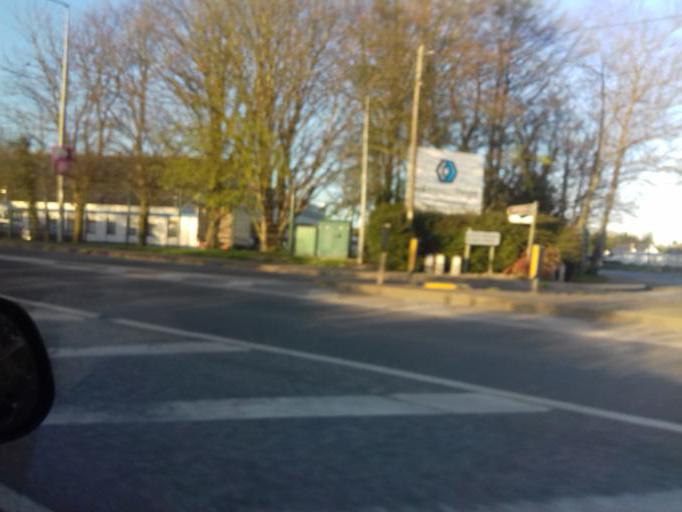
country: IE
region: Leinster
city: Lusk
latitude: 53.5022
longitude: -6.1932
